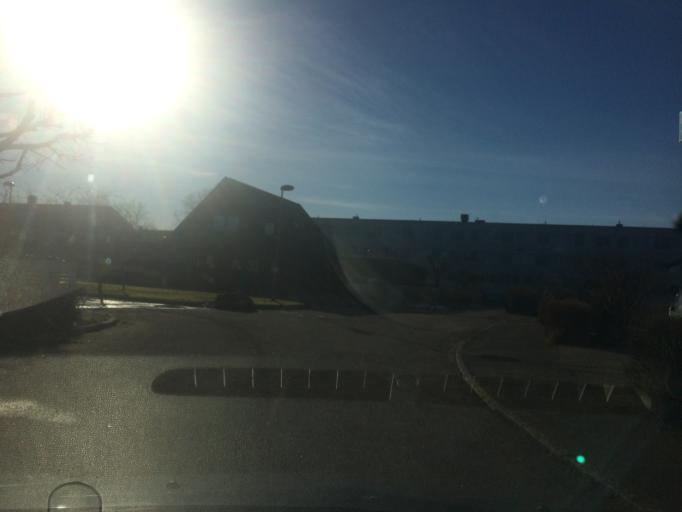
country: SE
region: Vaestra Goetaland
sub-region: Goteborg
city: Goeteborg
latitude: 57.7518
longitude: 11.9348
